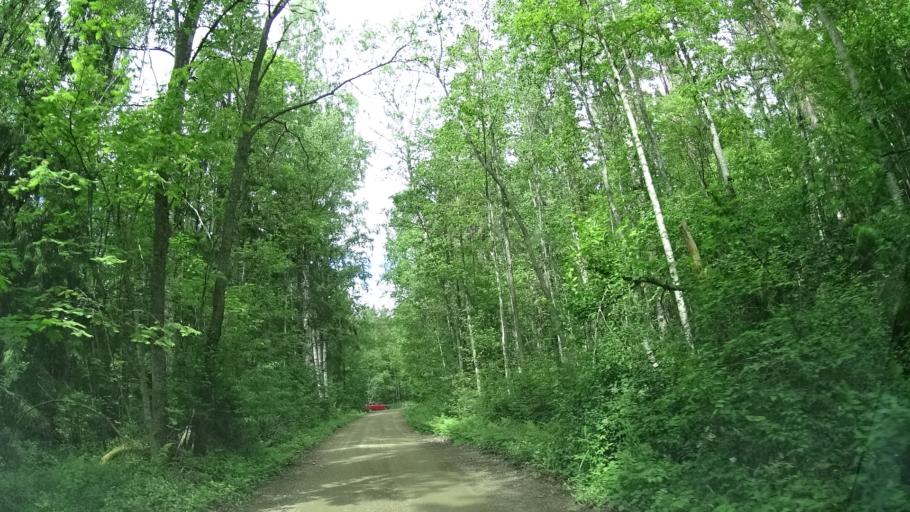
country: FI
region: Central Finland
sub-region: Joutsa
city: Luhanka
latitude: 61.6898
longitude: 25.6896
